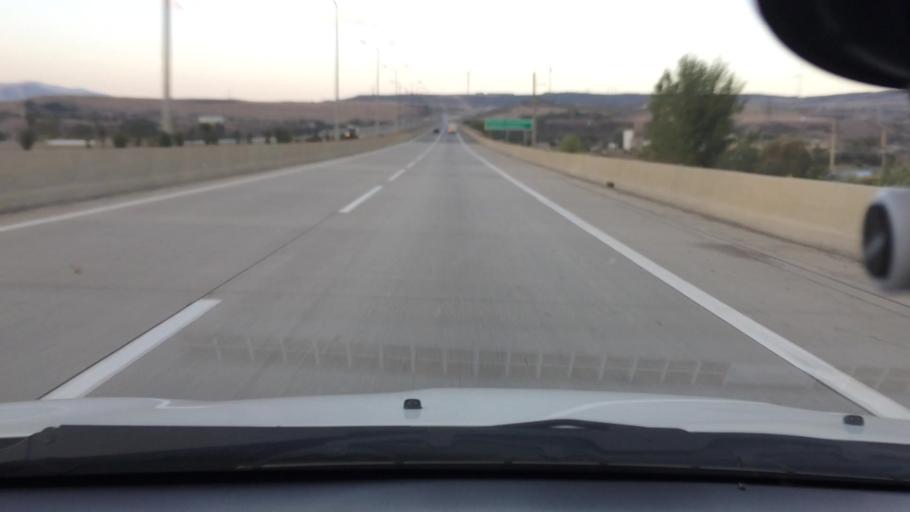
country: GE
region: Shida Kartli
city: Gori
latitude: 42.0175
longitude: 44.0920
